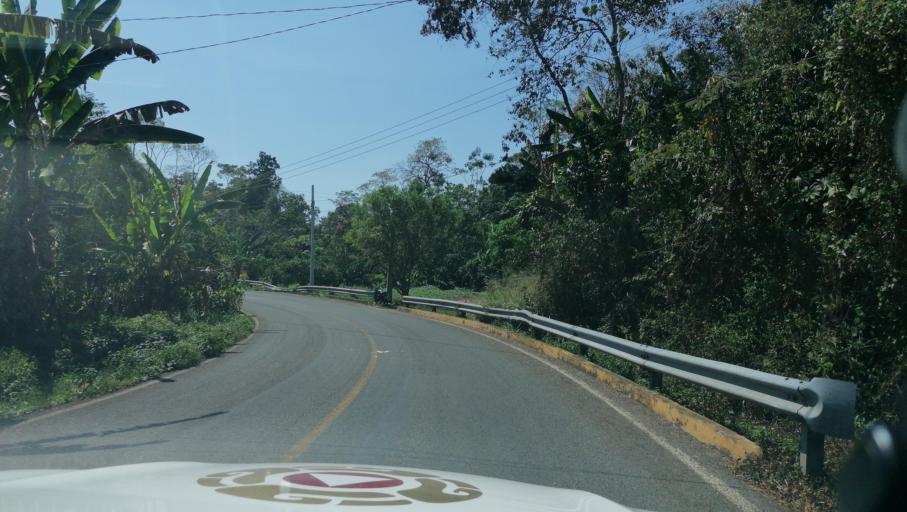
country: MX
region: Chiapas
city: Veinte de Noviembre
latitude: 15.0129
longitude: -92.2303
